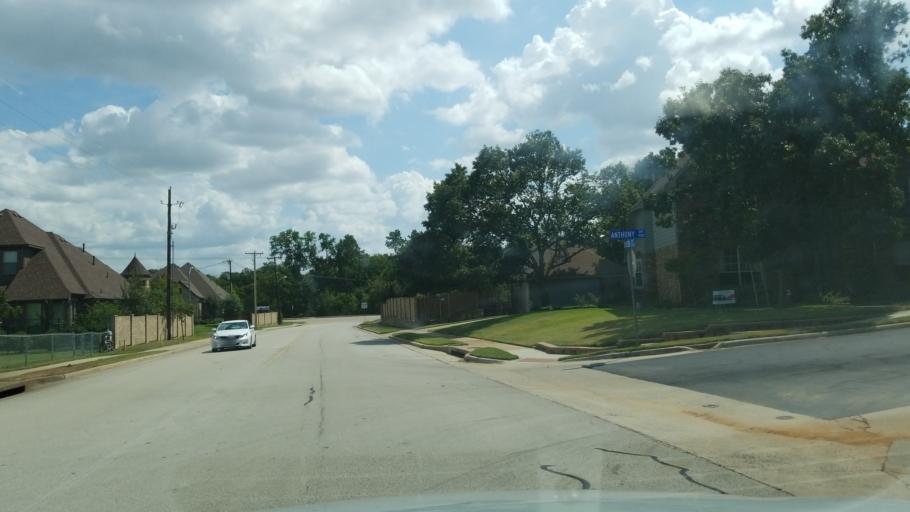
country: US
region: Texas
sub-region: Tarrant County
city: Euless
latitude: 32.8699
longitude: -97.0888
